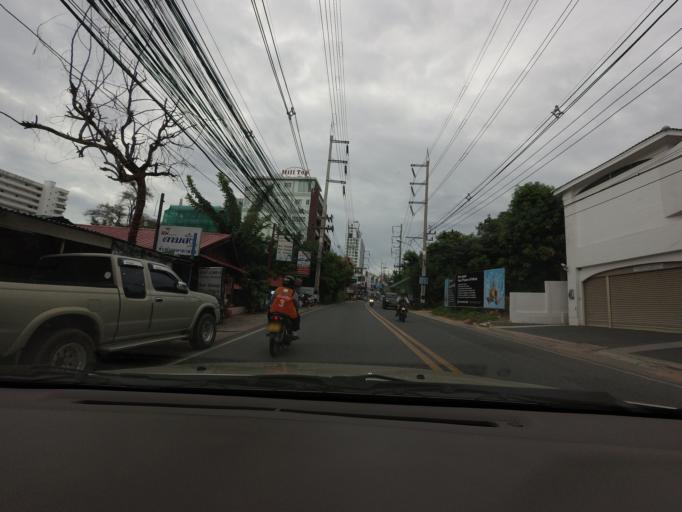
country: TH
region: Chon Buri
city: Phatthaya
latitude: 12.9146
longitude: 100.8669
